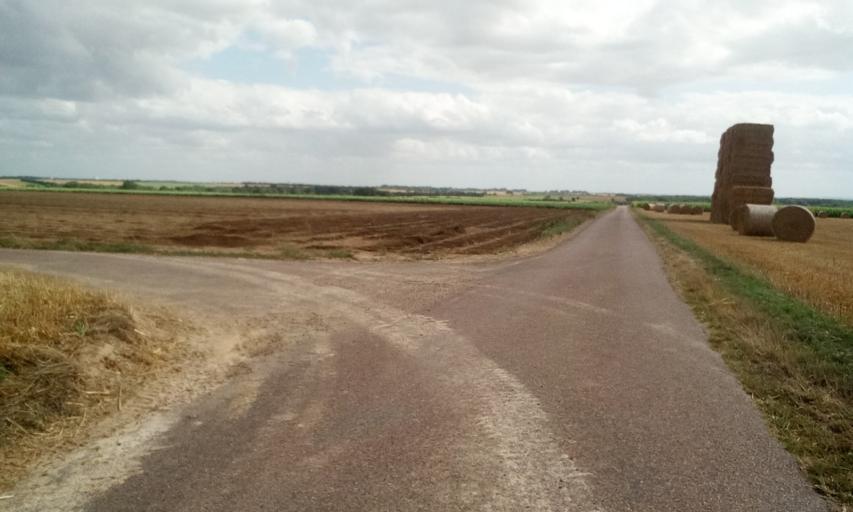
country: FR
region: Lower Normandy
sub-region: Departement du Calvados
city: Ver-sur-Mer
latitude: 49.3029
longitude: -0.5073
